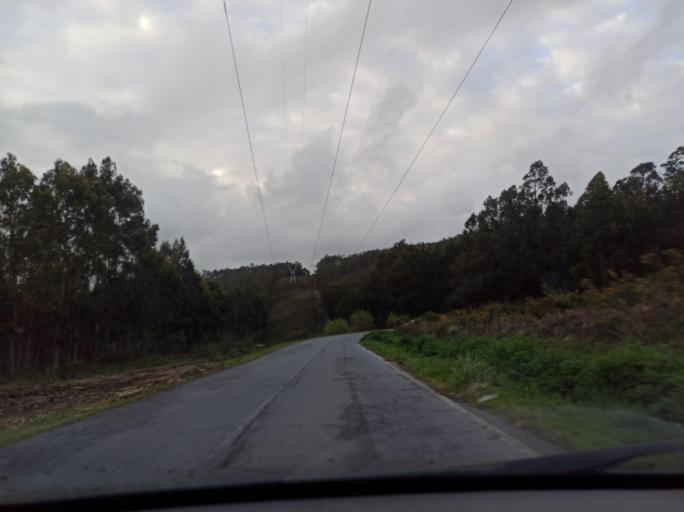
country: ES
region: Galicia
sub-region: Provincia da Coruna
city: Culleredo
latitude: 43.3008
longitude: -8.4330
